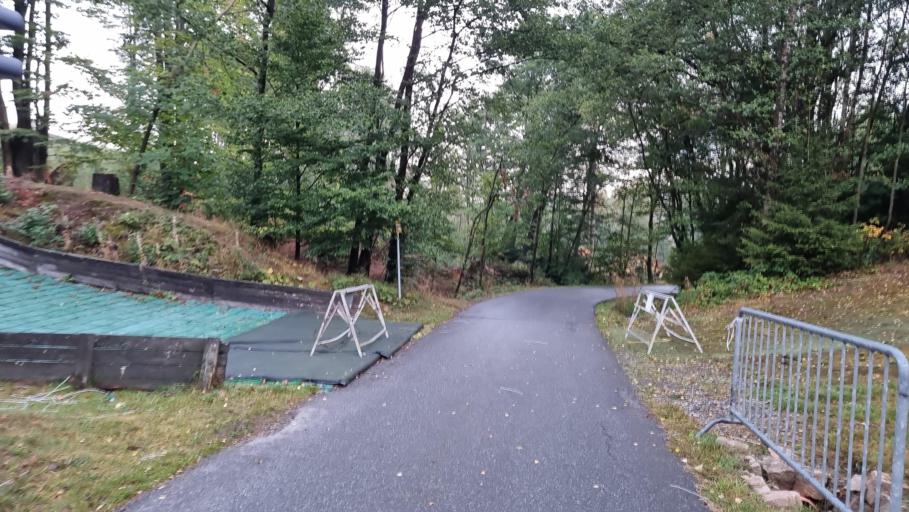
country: DE
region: Lower Saxony
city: Braunlage
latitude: 51.7394
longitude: 10.6118
